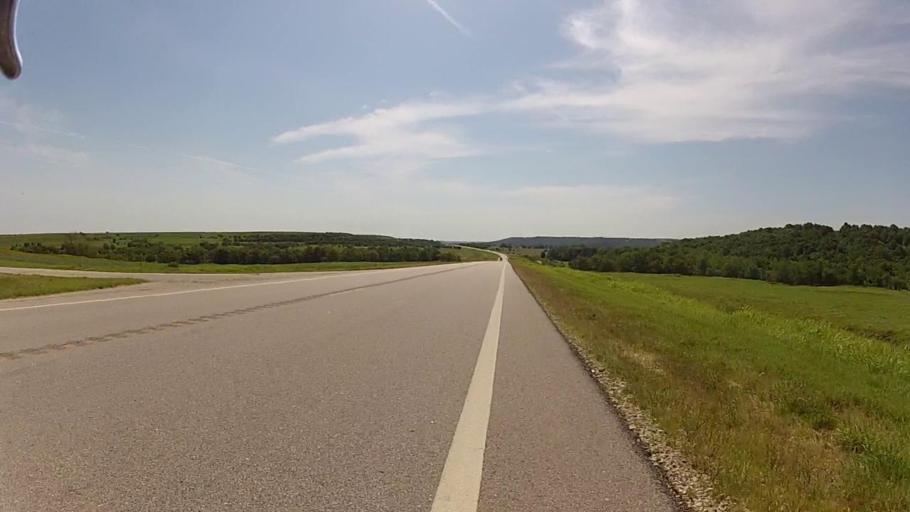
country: US
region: Kansas
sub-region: Chautauqua County
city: Sedan
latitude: 37.1103
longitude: -96.5923
